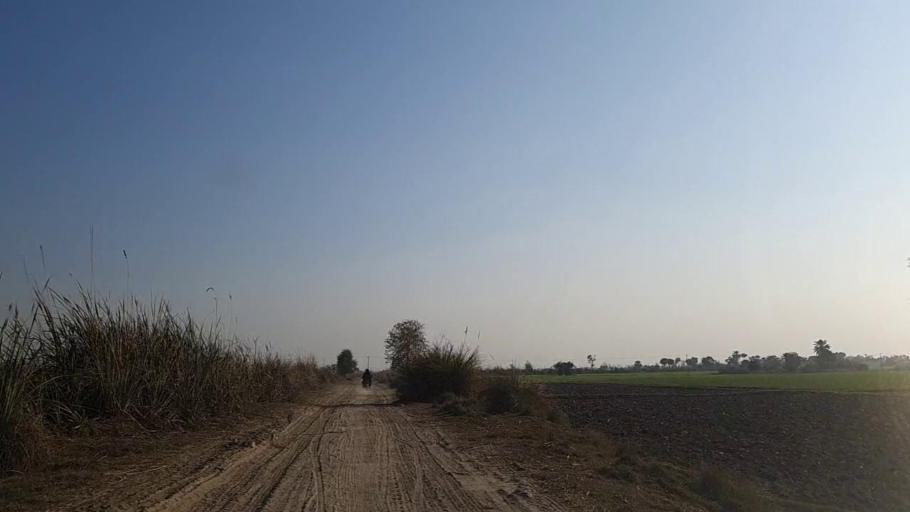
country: PK
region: Sindh
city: Daur
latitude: 26.4385
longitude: 68.3519
